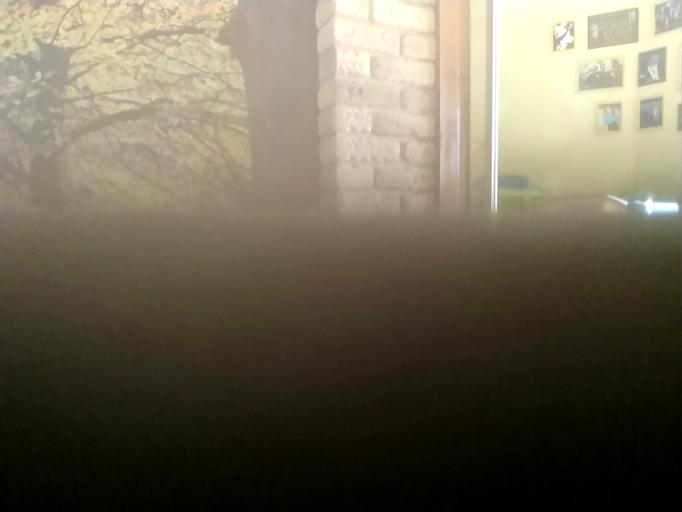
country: RU
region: Kaluga
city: Yukhnov
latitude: 54.7588
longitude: 35.0293
